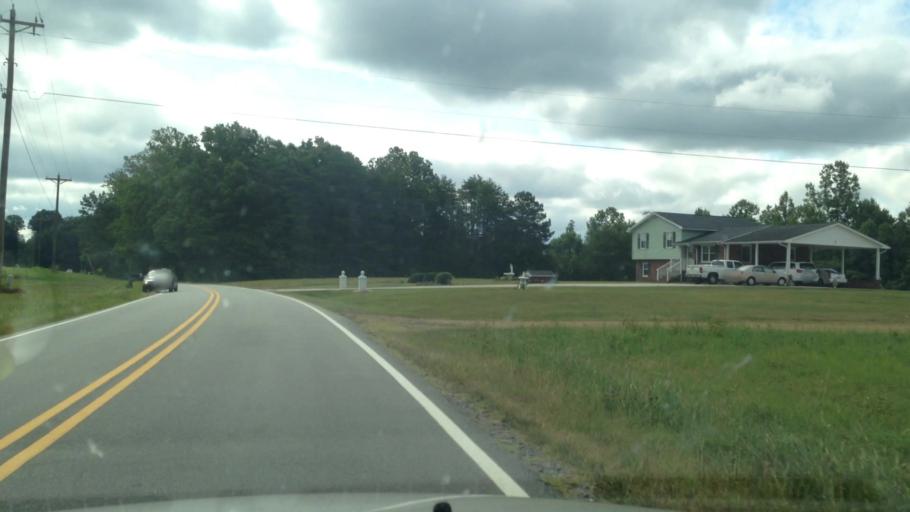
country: US
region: North Carolina
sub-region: Rockingham County
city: Mayodan
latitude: 36.3932
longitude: -80.0132
